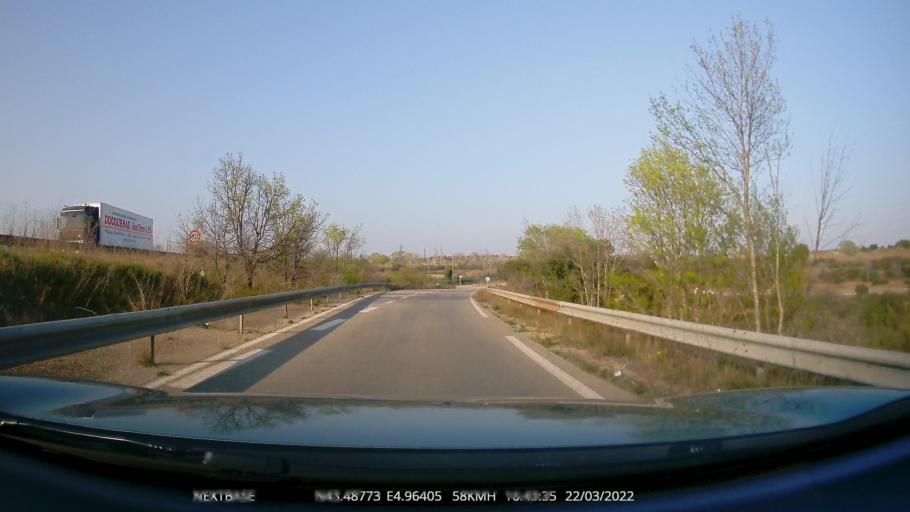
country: FR
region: Provence-Alpes-Cote d'Azur
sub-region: Departement des Bouches-du-Rhone
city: Istres
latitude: 43.4878
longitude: 4.9641
